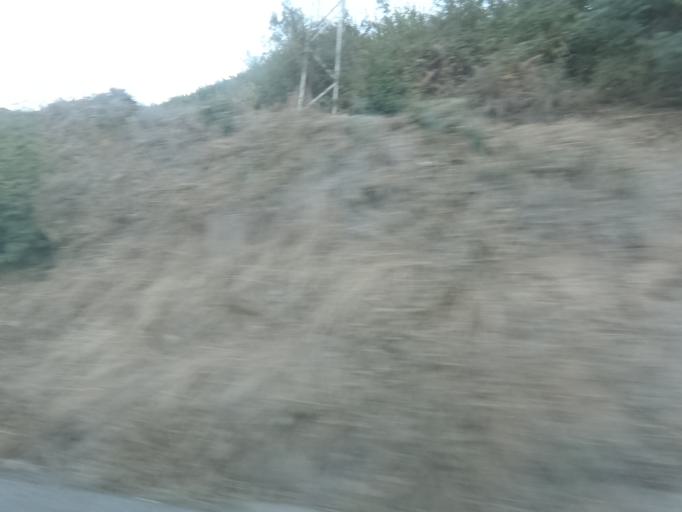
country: PT
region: Vila Real
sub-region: Peso da Regua
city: Peso da Regua
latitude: 41.1336
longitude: -7.7450
